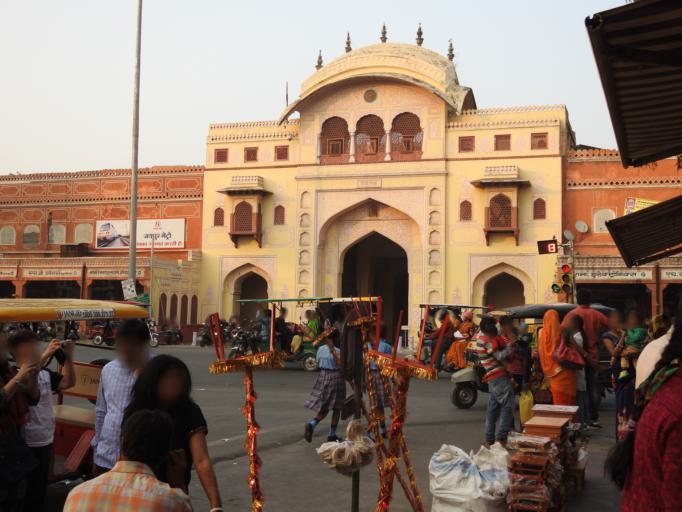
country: IN
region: Rajasthan
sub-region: Jaipur
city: Jaipur
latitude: 26.9236
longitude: 75.8226
